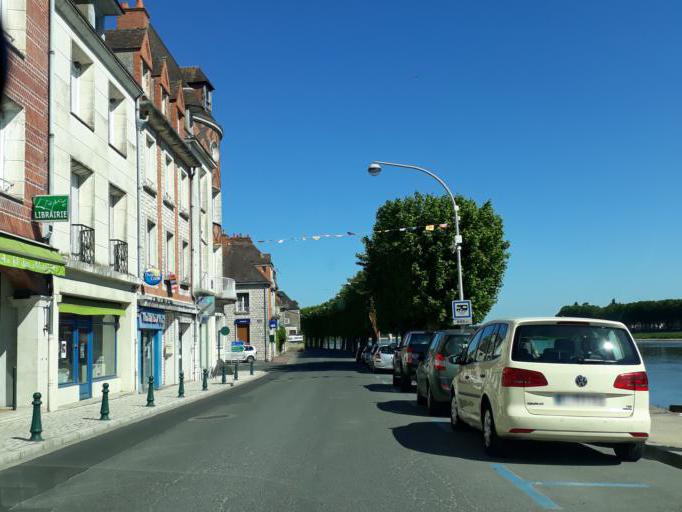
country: FR
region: Centre
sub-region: Departement du Loiret
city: Gien
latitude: 47.6836
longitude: 2.6323
